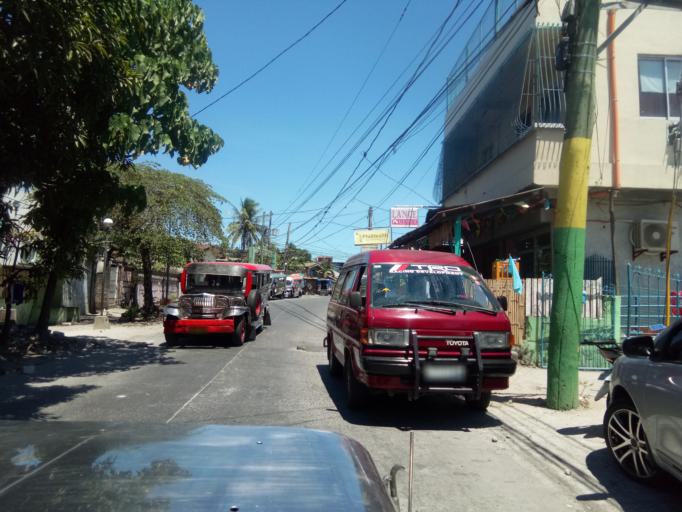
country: PH
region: Calabarzon
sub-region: Province of Cavite
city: Dasmarinas
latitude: 14.3220
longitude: 120.9672
